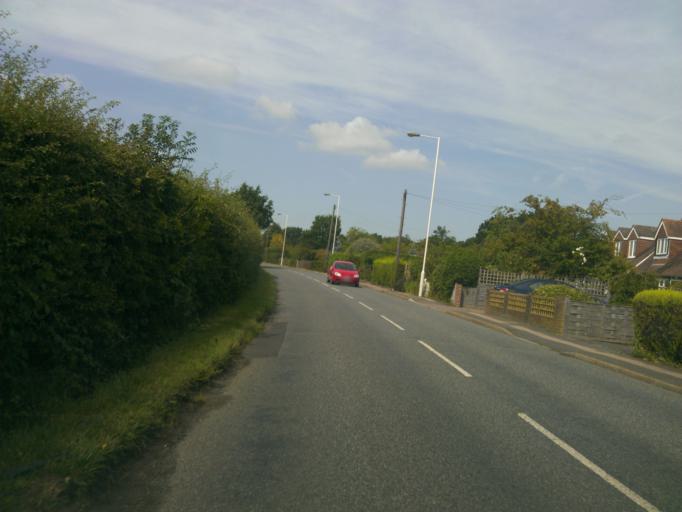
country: GB
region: England
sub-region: Kent
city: Tonbridge
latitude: 51.2113
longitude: 0.2457
